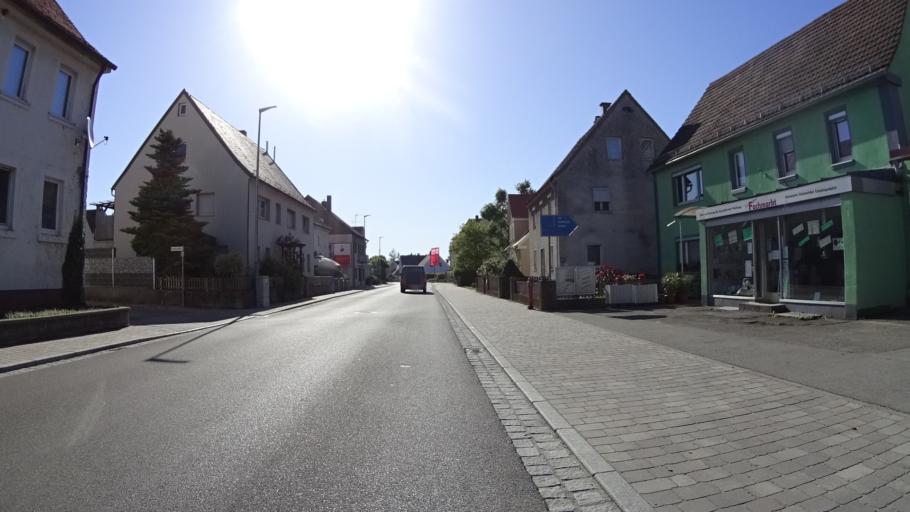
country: DE
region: Bavaria
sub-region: Regierungsbezirk Mittelfranken
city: Arberg
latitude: 49.1581
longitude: 10.5523
